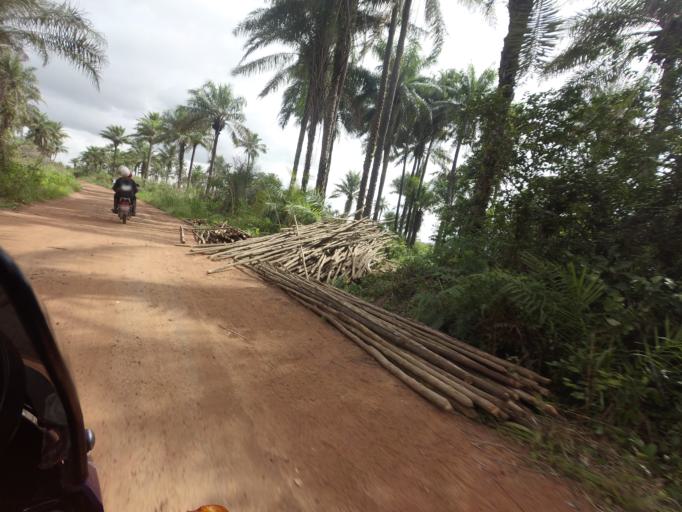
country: SL
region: Northern Province
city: Kambia
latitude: 9.0932
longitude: -13.0154
